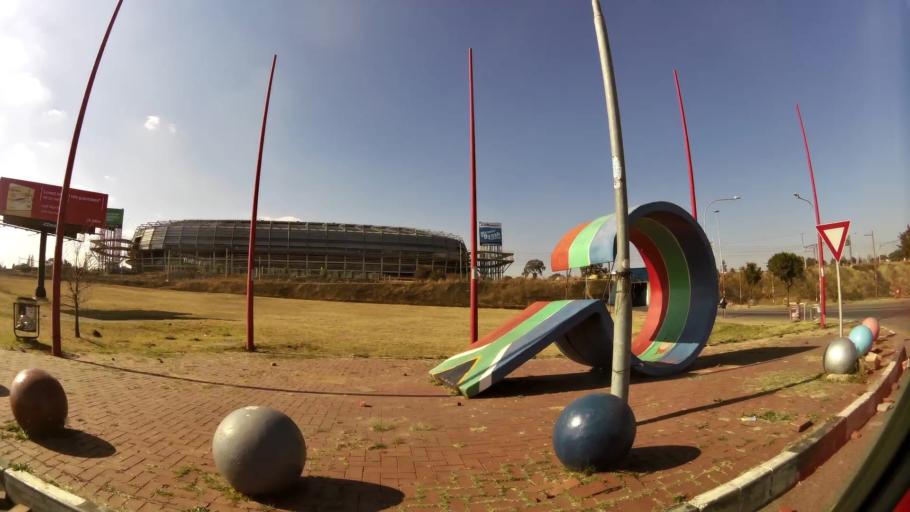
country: ZA
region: Gauteng
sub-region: City of Johannesburg Metropolitan Municipality
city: Soweto
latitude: -26.2310
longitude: 27.9200
